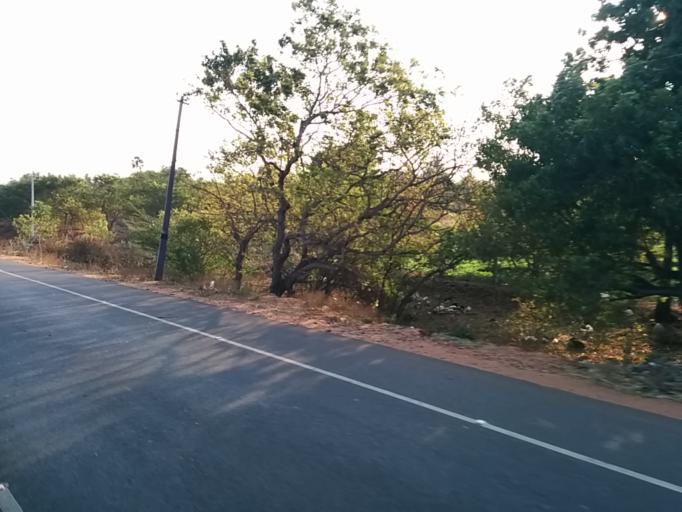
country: IN
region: Tamil Nadu
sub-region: Villupuram
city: Auroville
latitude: 11.9985
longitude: 79.8521
